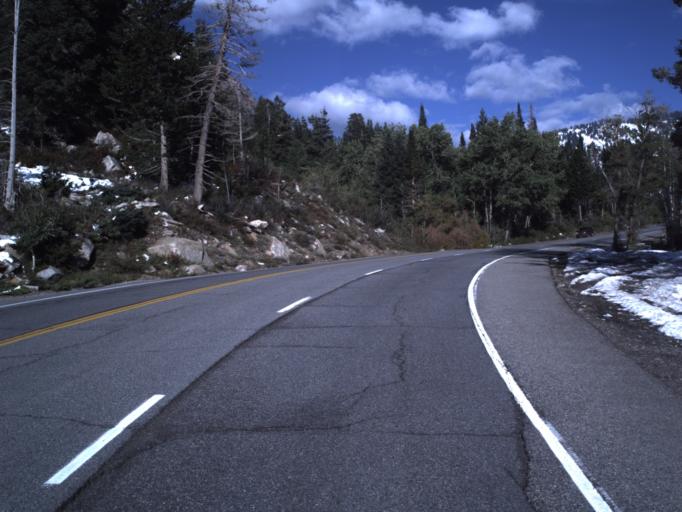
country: US
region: Utah
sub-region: Salt Lake County
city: Granite
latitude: 40.5752
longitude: -111.6854
